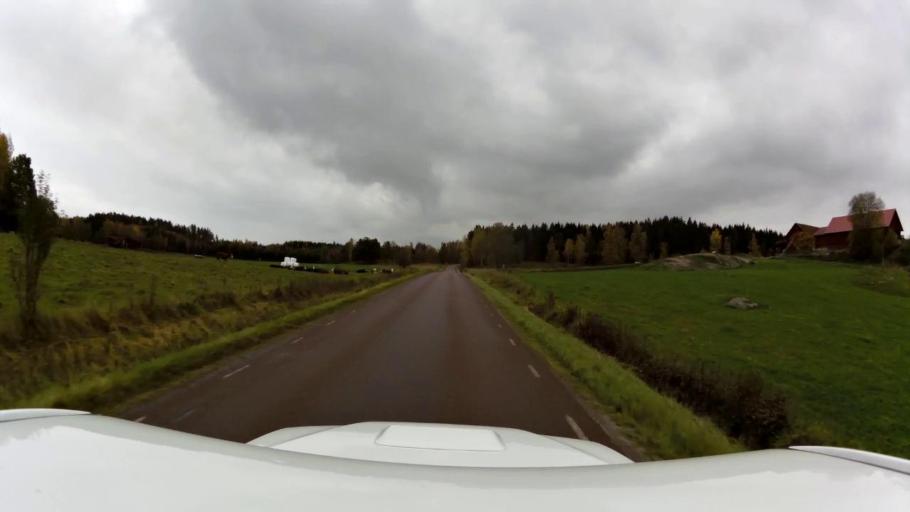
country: SE
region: OEstergoetland
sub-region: Linkopings Kommun
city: Ljungsbro
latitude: 58.5423
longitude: 15.5259
